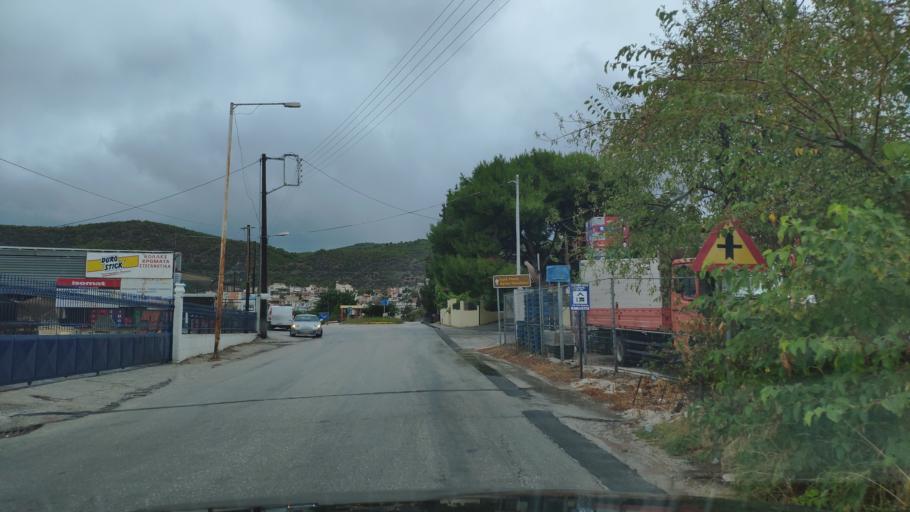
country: GR
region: Peloponnese
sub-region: Nomos Korinthias
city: Perachora
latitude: 38.0248
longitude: 22.9482
